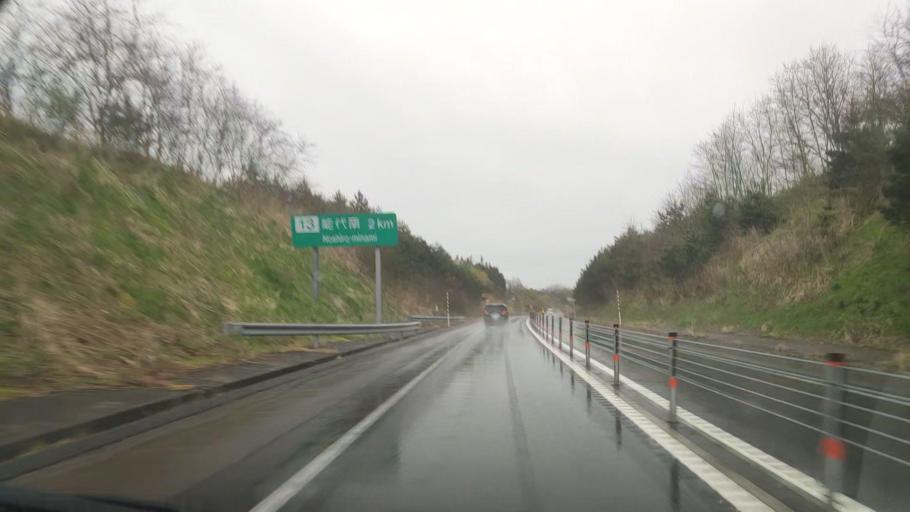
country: JP
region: Akita
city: Noshiromachi
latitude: 40.1634
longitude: 140.0444
